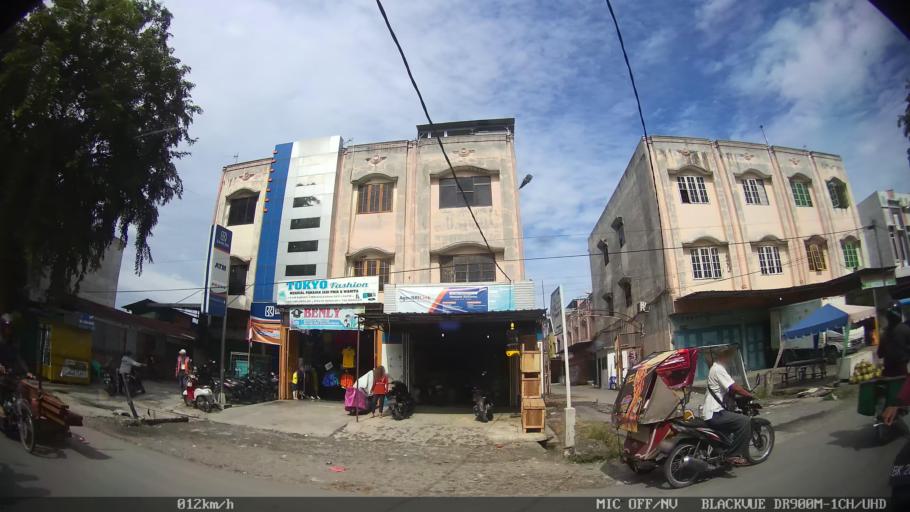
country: ID
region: North Sumatra
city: Sunggal
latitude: 3.6040
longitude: 98.6081
